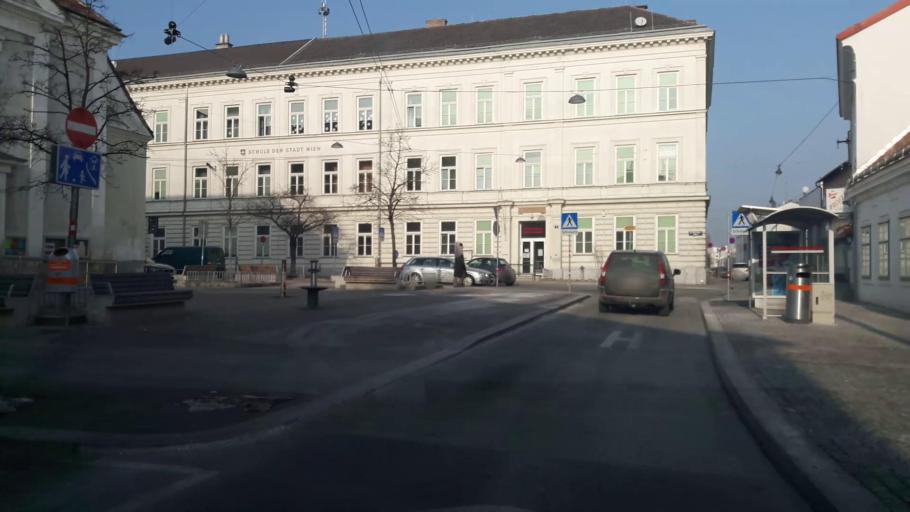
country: AT
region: Lower Austria
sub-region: Politischer Bezirk Modling
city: Perchtoldsdorf
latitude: 48.1472
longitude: 16.2949
